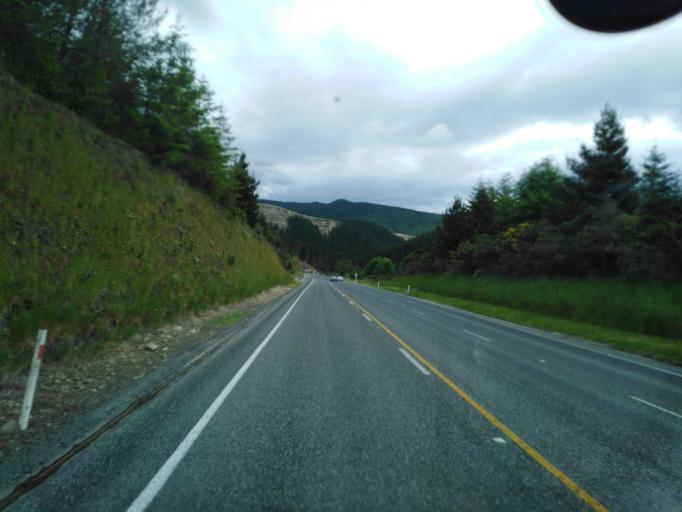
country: NZ
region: Tasman
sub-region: Tasman District
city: Wakefield
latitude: -41.4849
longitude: 172.9037
